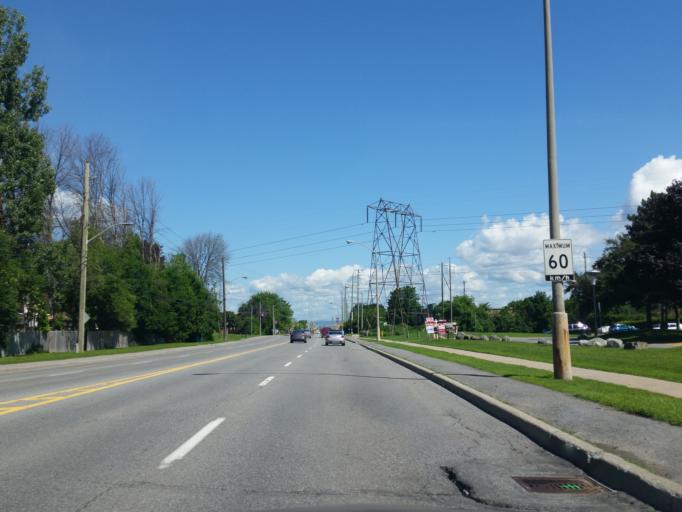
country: CA
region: Ontario
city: Bells Corners
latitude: 45.3180
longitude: -75.8307
